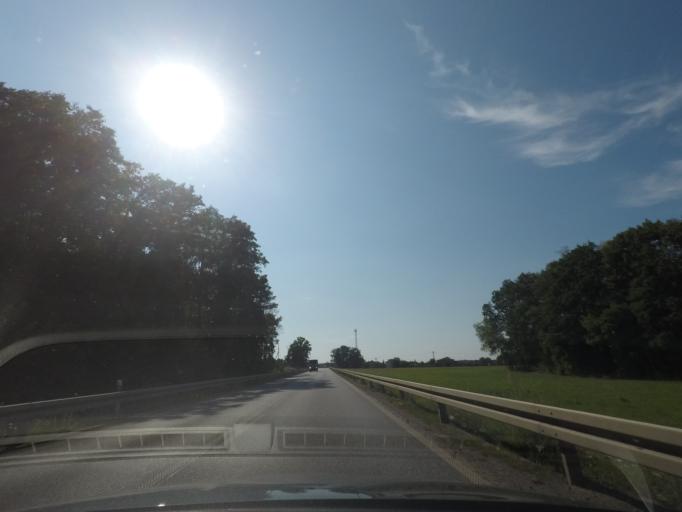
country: PL
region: Silesian Voivodeship
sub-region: Powiat pszczynski
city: Suszec
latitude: 50.0291
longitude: 18.7972
